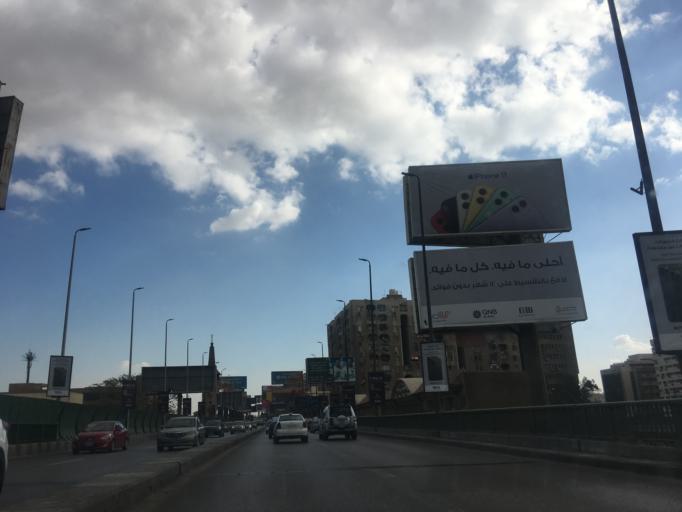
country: EG
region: Muhafazat al Qahirah
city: Cairo
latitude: 30.0744
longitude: 31.2859
